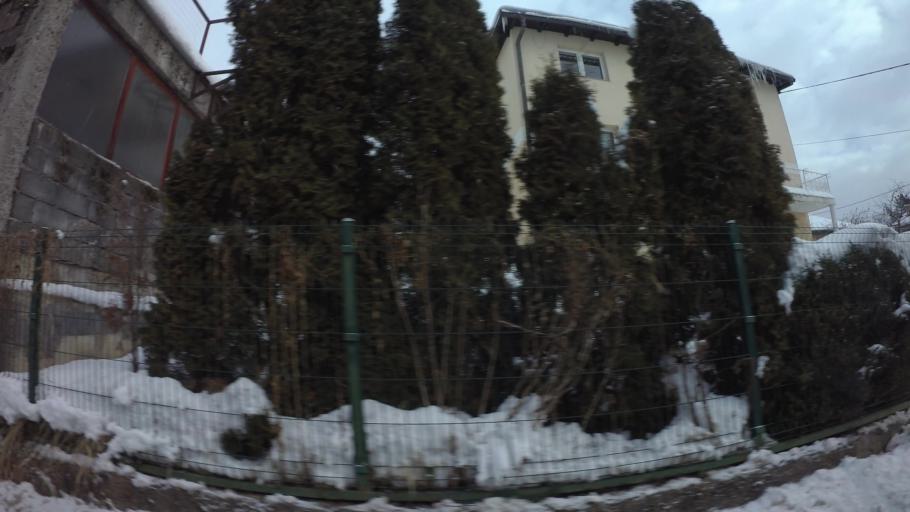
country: BA
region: Federation of Bosnia and Herzegovina
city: Kobilja Glava
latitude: 43.8704
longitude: 18.4412
